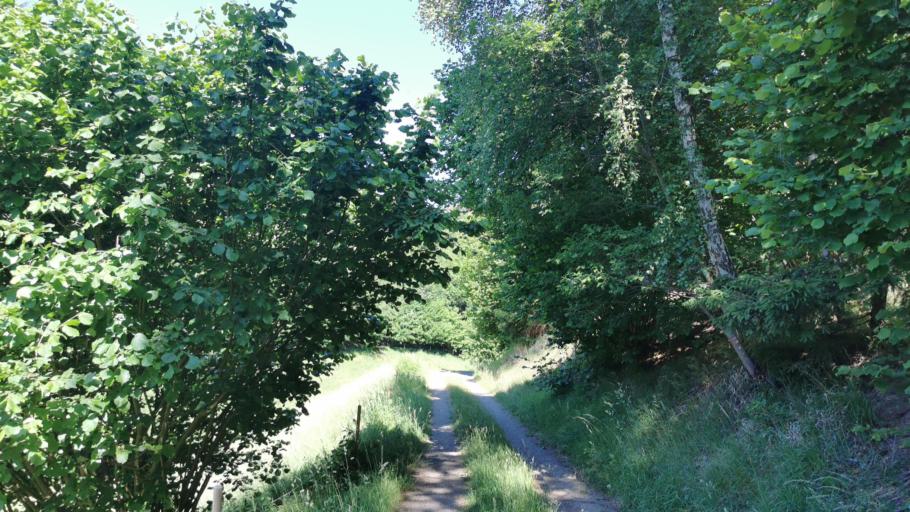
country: DE
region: Thuringia
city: Probstzella
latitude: 50.5438
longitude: 11.3990
